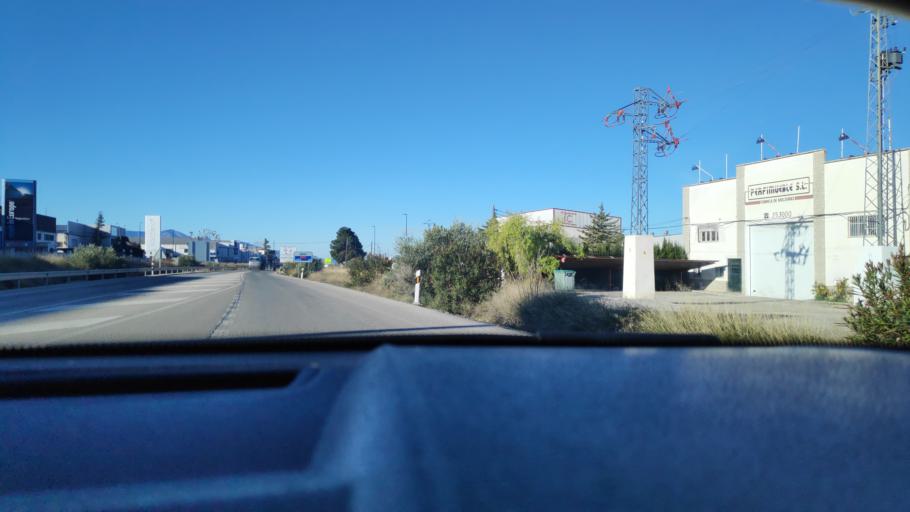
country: ES
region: Andalusia
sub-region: Provincia de Jaen
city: Mancha Real
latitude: 37.8069
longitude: -3.6135
